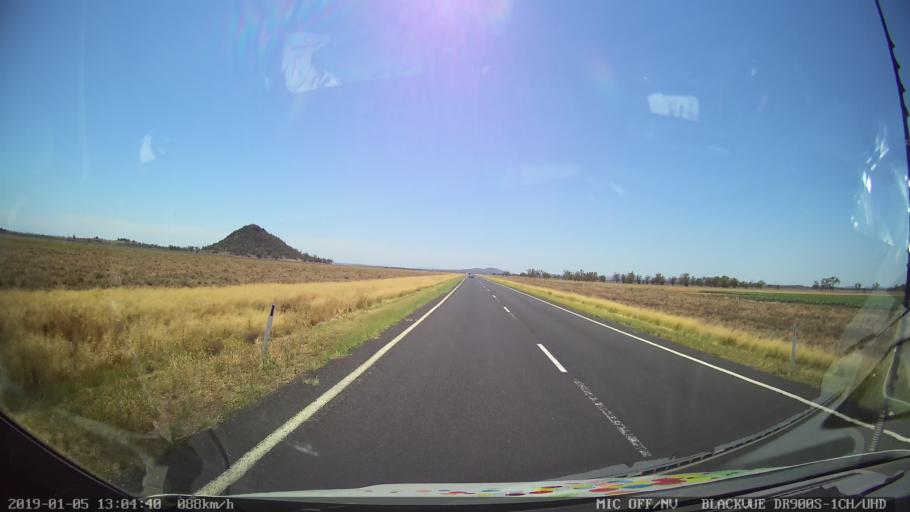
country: AU
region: New South Wales
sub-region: Gunnedah
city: Gunnedah
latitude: -31.1013
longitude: 149.8431
